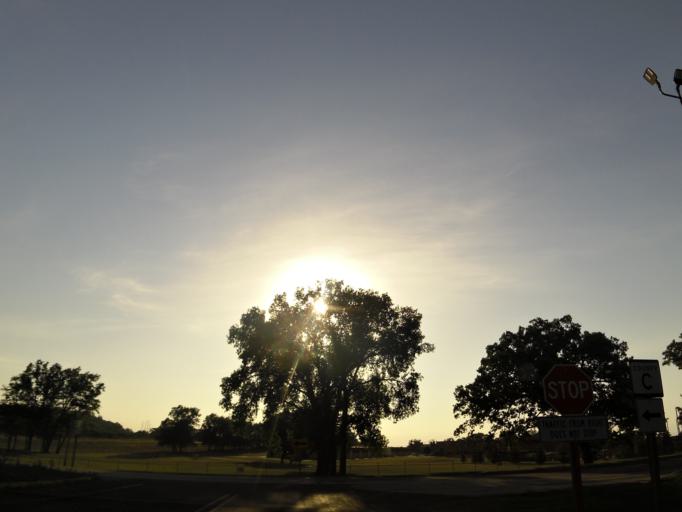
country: US
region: Wisconsin
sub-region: Juneau County
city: New Lisbon
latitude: 43.9231
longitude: -90.2614
